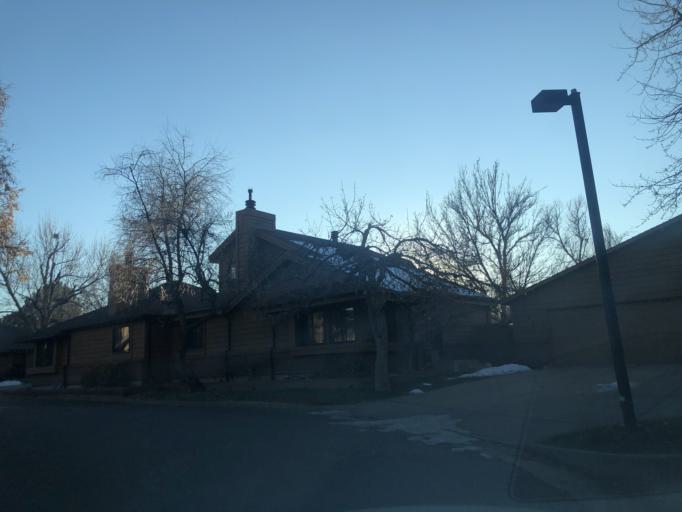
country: US
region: Colorado
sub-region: Adams County
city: Aurora
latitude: 39.7156
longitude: -104.8162
